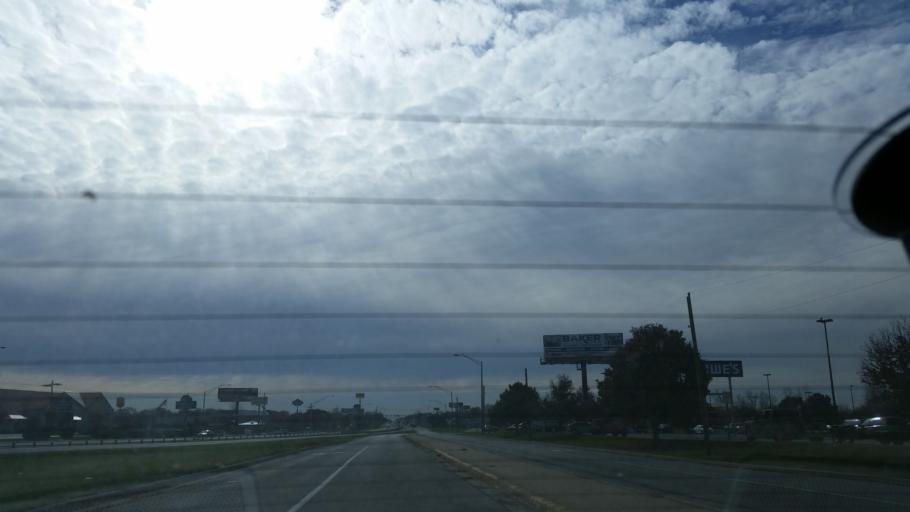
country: US
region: Indiana
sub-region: Howard County
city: Indian Heights
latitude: 40.4403
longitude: -86.1271
